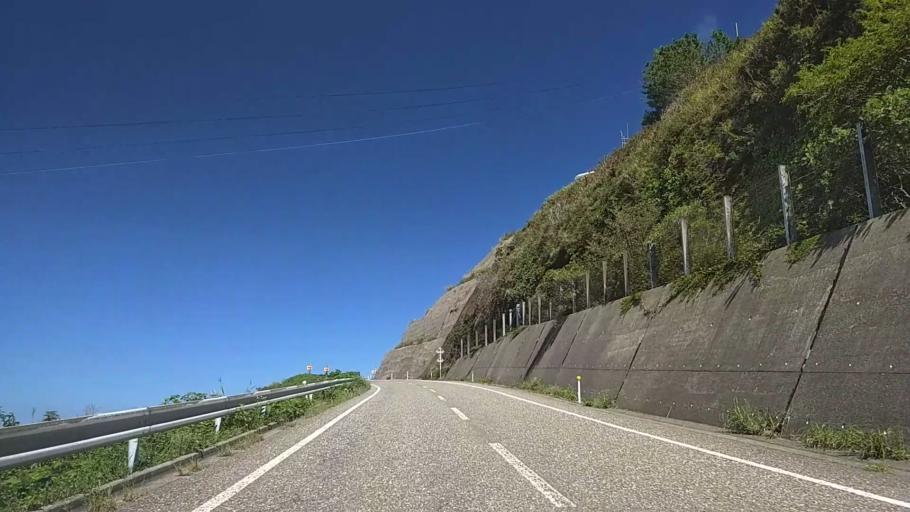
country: JP
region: Niigata
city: Joetsu
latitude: 37.1702
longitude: 138.0954
